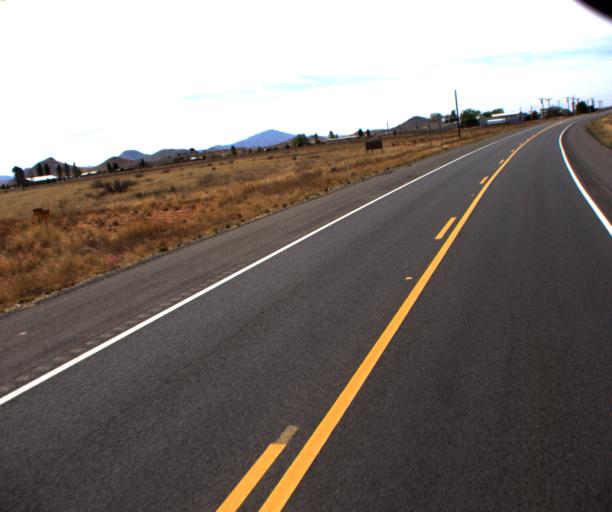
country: US
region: Arizona
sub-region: Cochise County
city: Willcox
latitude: 31.8900
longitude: -109.6954
